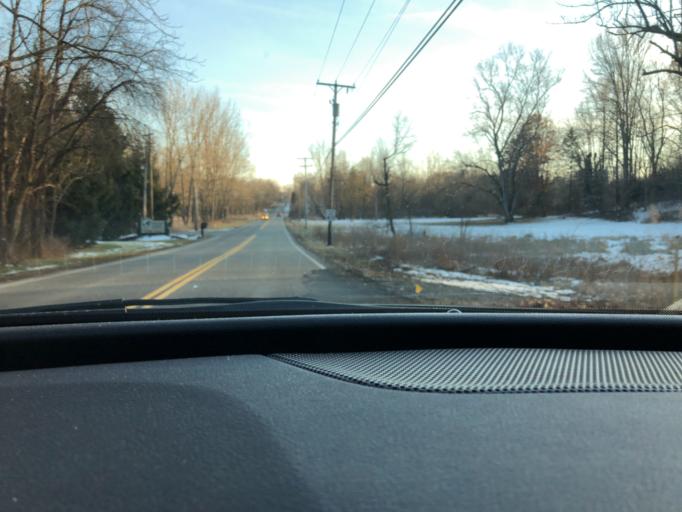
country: US
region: Ohio
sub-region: Stark County
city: Perry Heights
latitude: 40.8052
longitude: -81.4650
